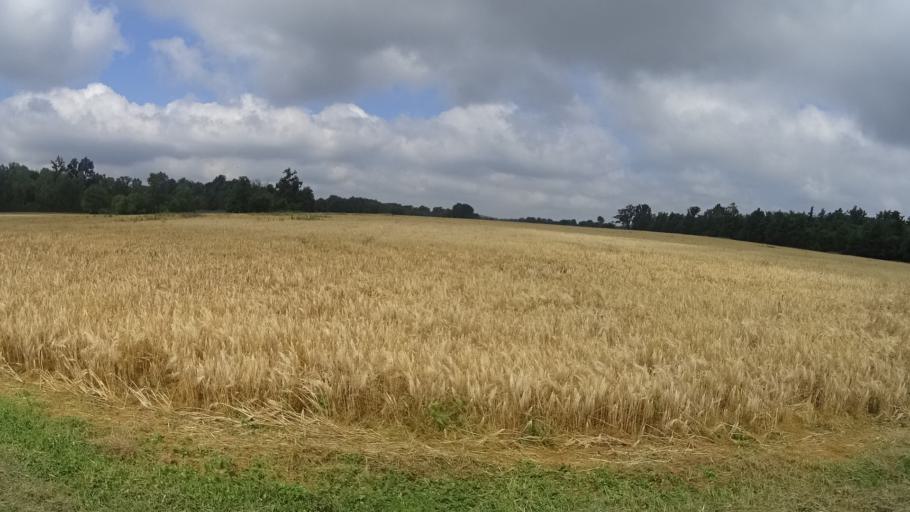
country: US
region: Ohio
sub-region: Huron County
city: Wakeman
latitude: 41.3296
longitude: -82.4386
